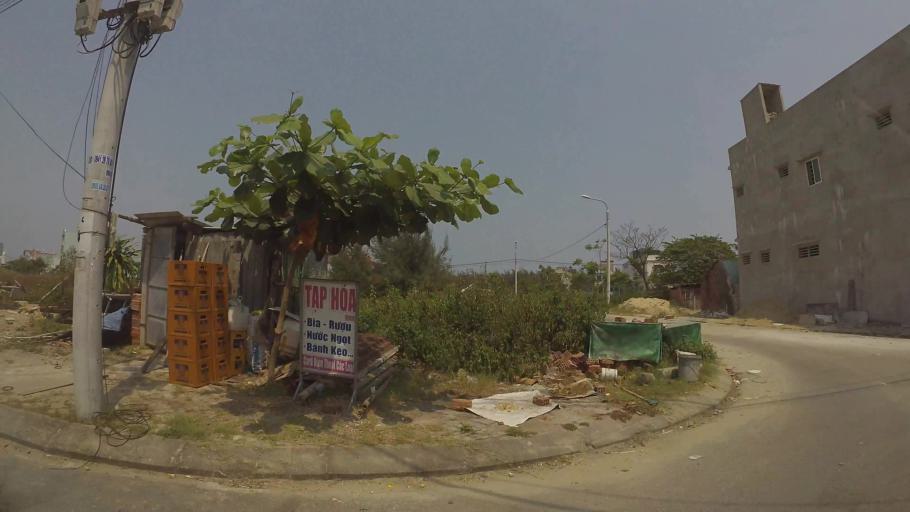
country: VN
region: Da Nang
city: Ngu Hanh Son
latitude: 15.9955
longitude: 108.2660
